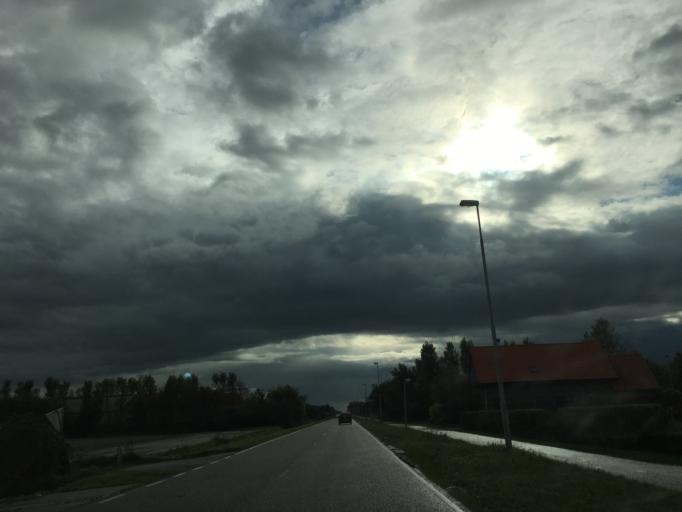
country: NL
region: North Holland
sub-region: Gemeente Den Helder
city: Den Helder
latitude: 52.9204
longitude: 4.7547
